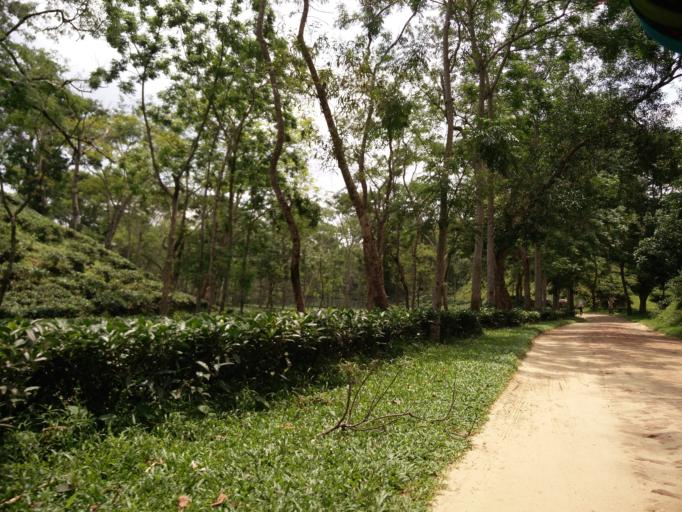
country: IN
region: Tripura
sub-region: Dhalai
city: Kamalpur
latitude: 24.3024
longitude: 91.7932
